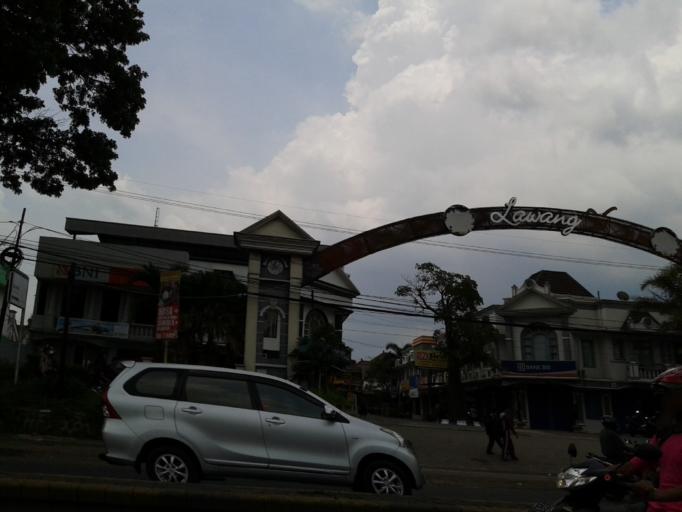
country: ID
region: East Java
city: Lawang
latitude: -7.8348
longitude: 112.6978
